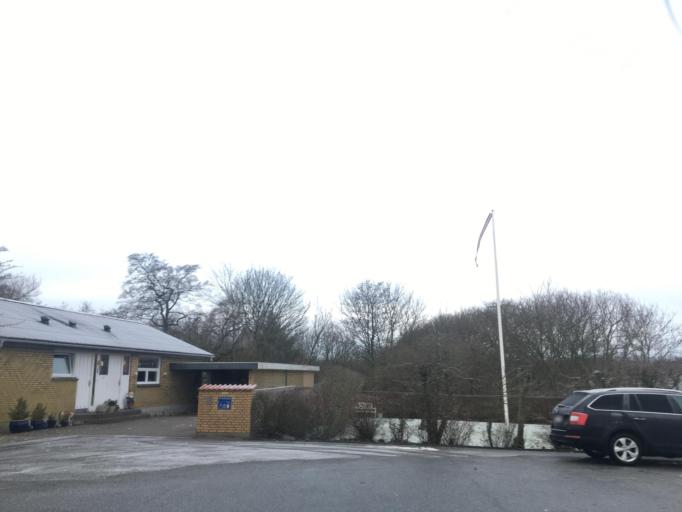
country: DK
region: North Denmark
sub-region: Thisted Kommune
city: Hurup
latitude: 56.7537
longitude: 8.4293
